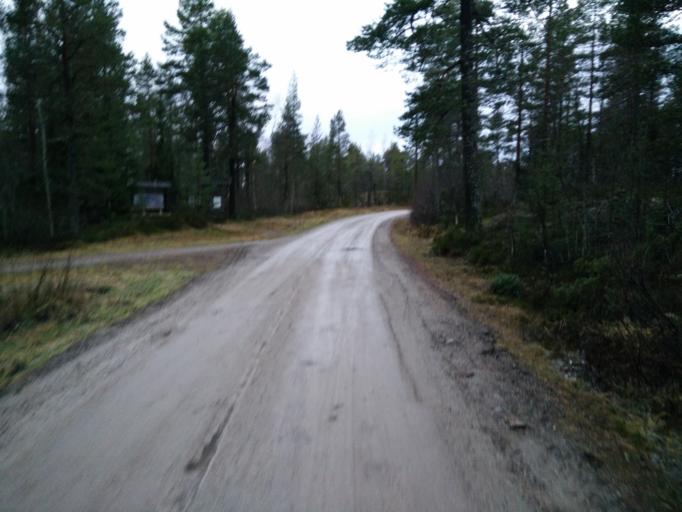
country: SE
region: Vaesternorrland
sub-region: Sundsvalls Kommun
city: Sundsvall
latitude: 62.3669
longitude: 17.3124
